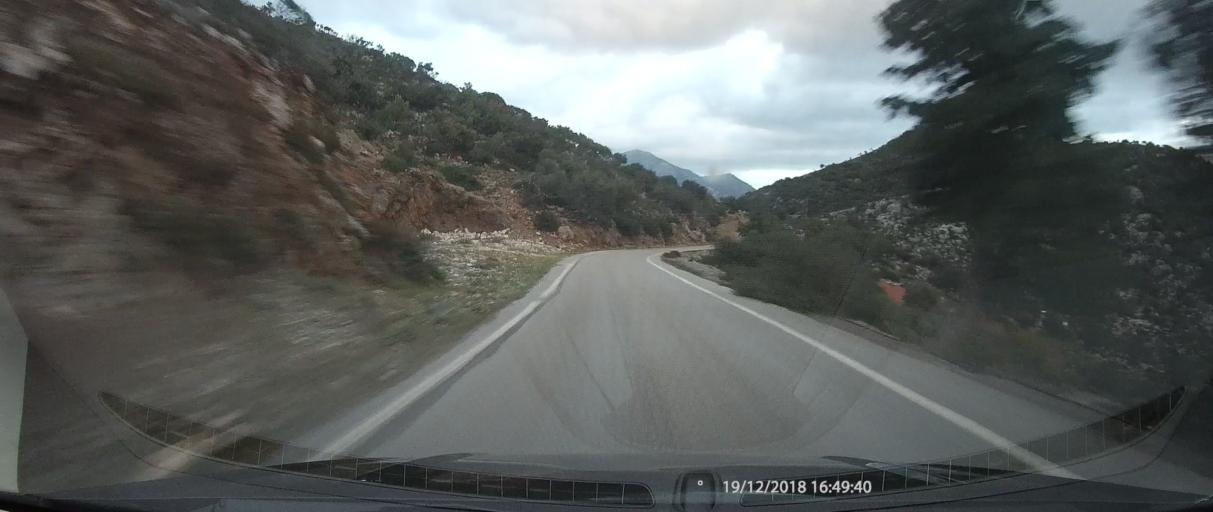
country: GR
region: Peloponnese
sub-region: Nomos Lakonias
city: Sykea
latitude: 36.9481
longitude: 22.9960
